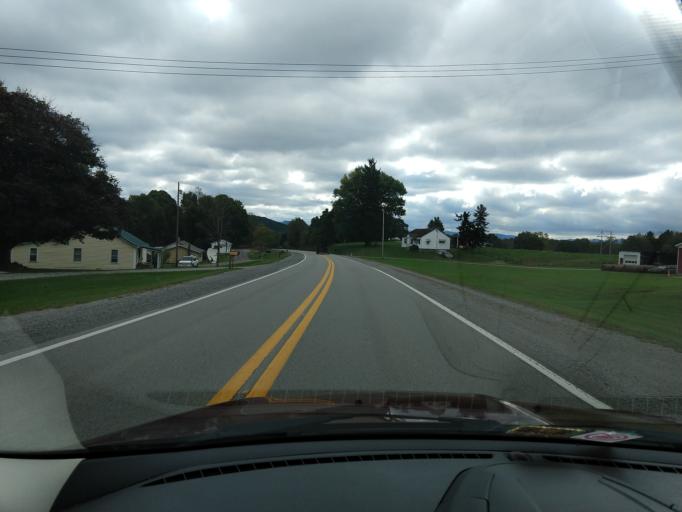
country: US
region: West Virginia
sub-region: Barbour County
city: Belington
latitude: 39.0608
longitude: -79.9696
